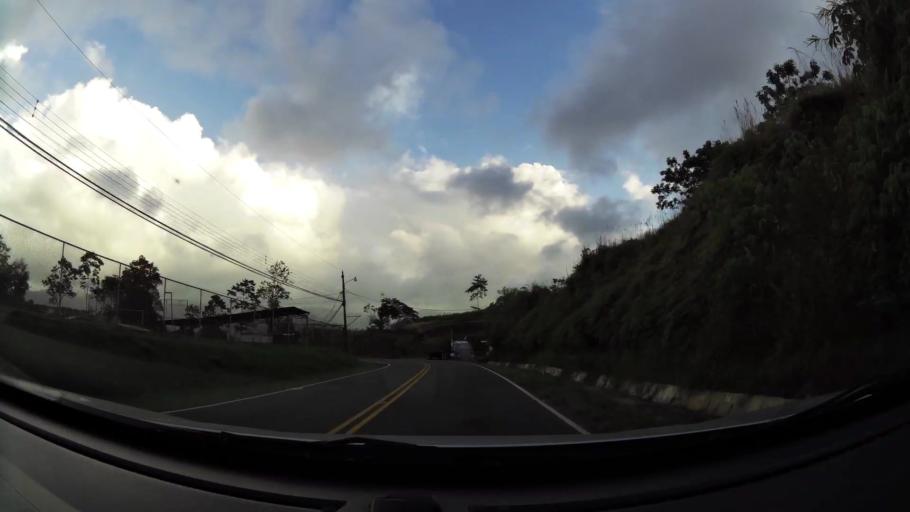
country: CR
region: Limon
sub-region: Canton de Siquirres
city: Siquirres
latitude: 9.9882
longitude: -83.5708
